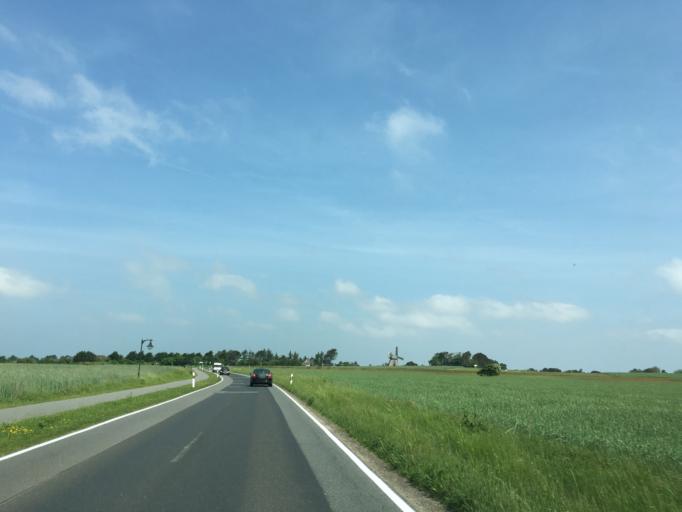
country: DE
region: Schleswig-Holstein
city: Nebel
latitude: 54.6443
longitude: 8.3547
